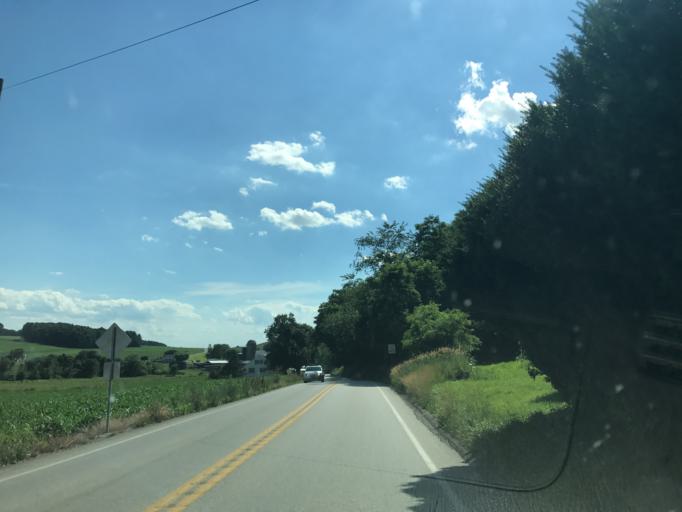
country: US
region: Pennsylvania
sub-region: York County
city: Glen Rock
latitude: 39.7397
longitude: -76.7849
